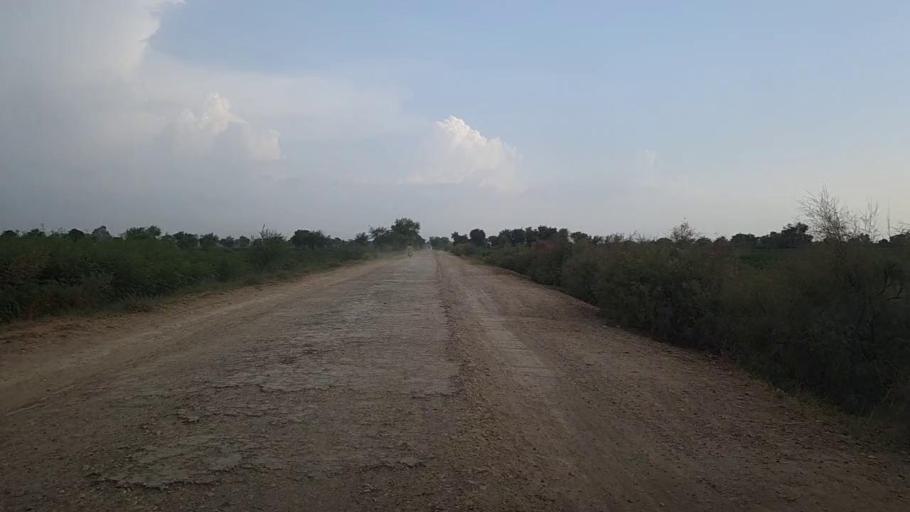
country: PK
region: Sindh
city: Khanpur
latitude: 27.8611
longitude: 69.4870
